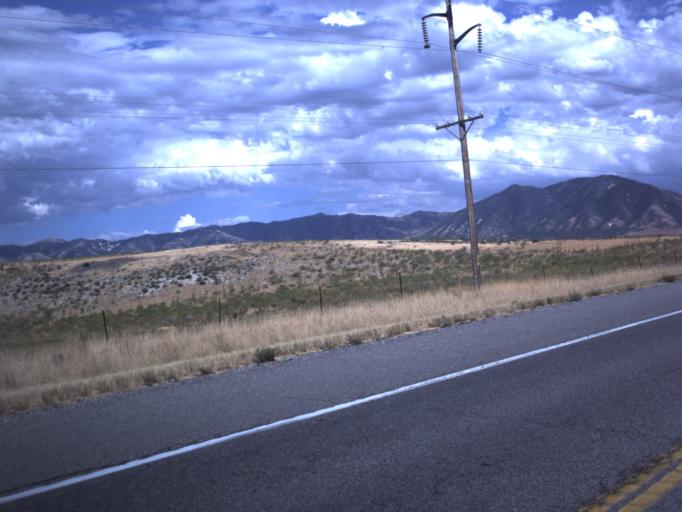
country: US
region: Utah
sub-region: Tooele County
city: Tooele
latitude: 40.5603
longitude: -112.3533
